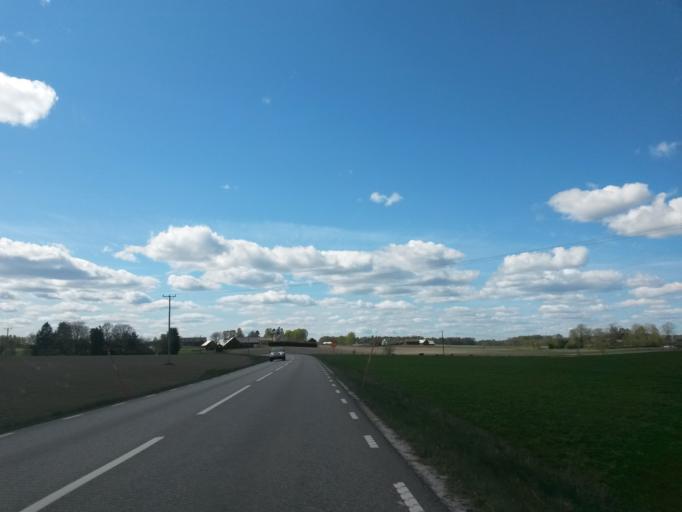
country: SE
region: Vaestra Goetaland
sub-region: Herrljunga Kommun
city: Herrljunga
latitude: 58.0723
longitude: 12.9885
